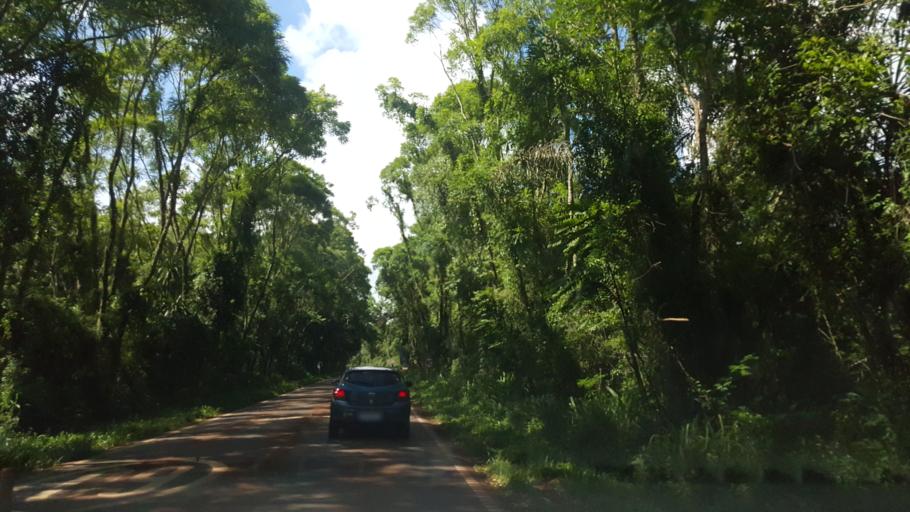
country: AR
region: Misiones
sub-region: Departamento de Iguazu
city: Puerto Iguazu
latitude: -25.7148
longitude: -54.4624
